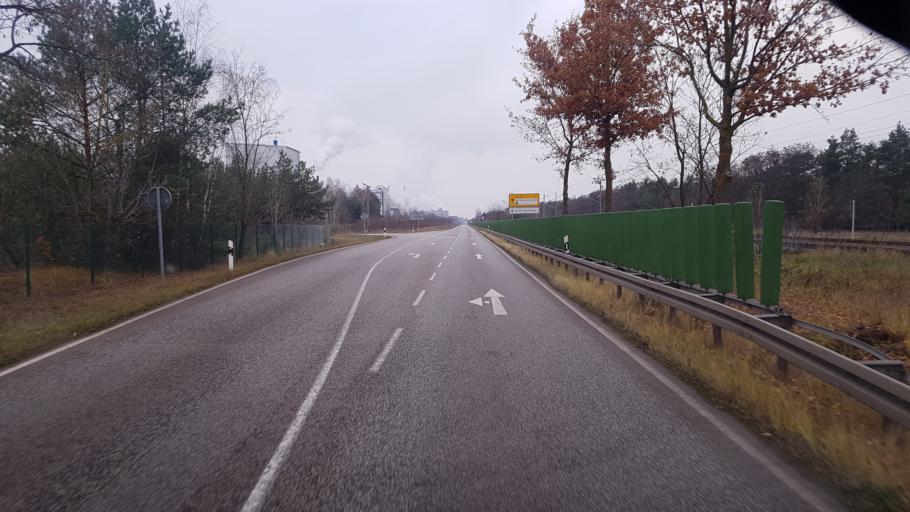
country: DE
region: Brandenburg
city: Eisenhuettenstadt
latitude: 52.1659
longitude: 14.6498
